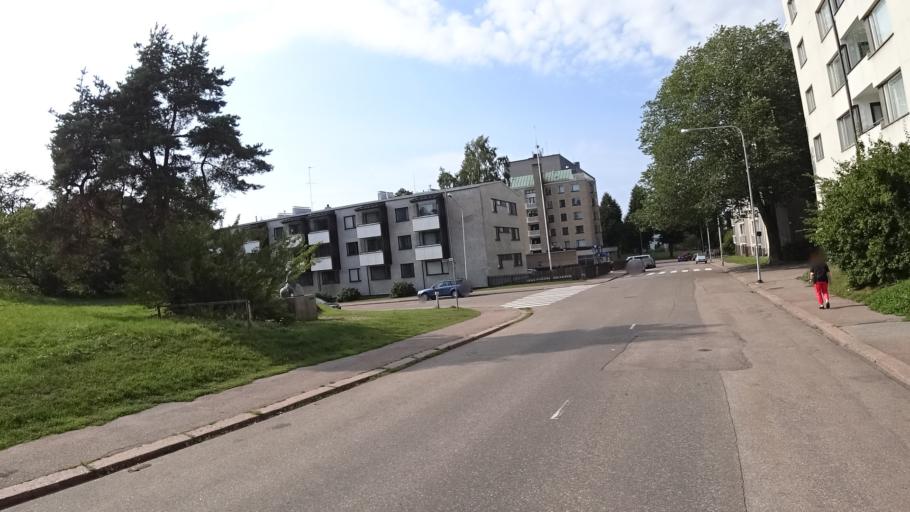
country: FI
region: Kymenlaakso
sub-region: Kotka-Hamina
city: Kotka
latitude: 60.4666
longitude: 26.9495
